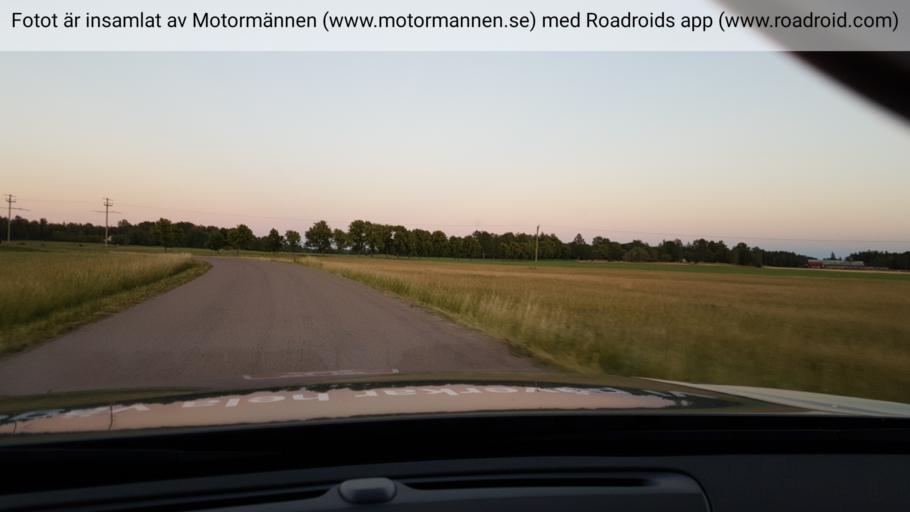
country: SE
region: Vaestmanland
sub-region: Hallstahammars Kommun
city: Kolback
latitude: 59.5265
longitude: 16.1773
